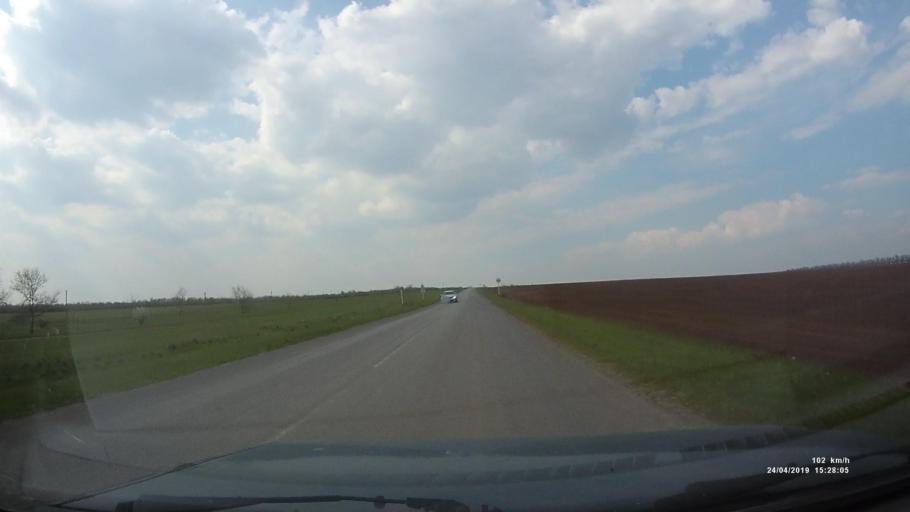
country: RU
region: Rostov
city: Remontnoye
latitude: 46.5739
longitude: 43.0210
